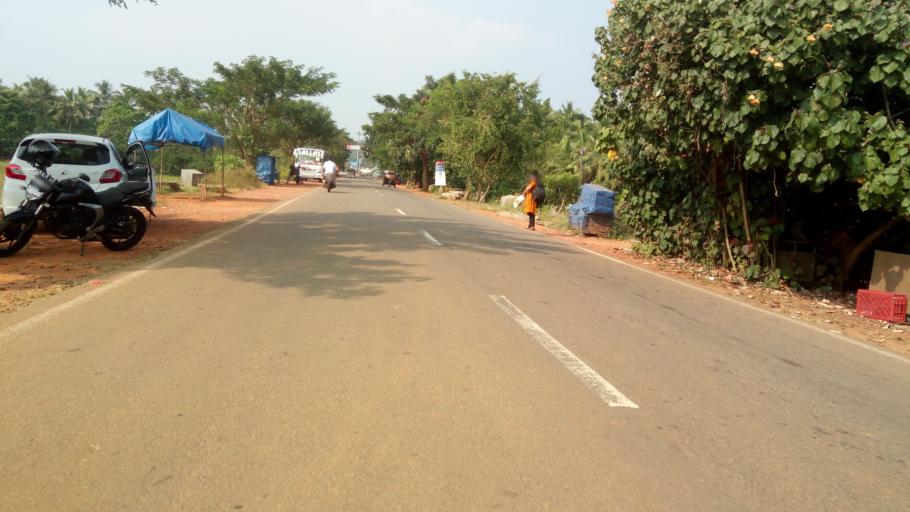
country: IN
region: Kerala
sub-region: Malappuram
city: Malappuram
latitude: 11.0021
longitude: 76.0145
